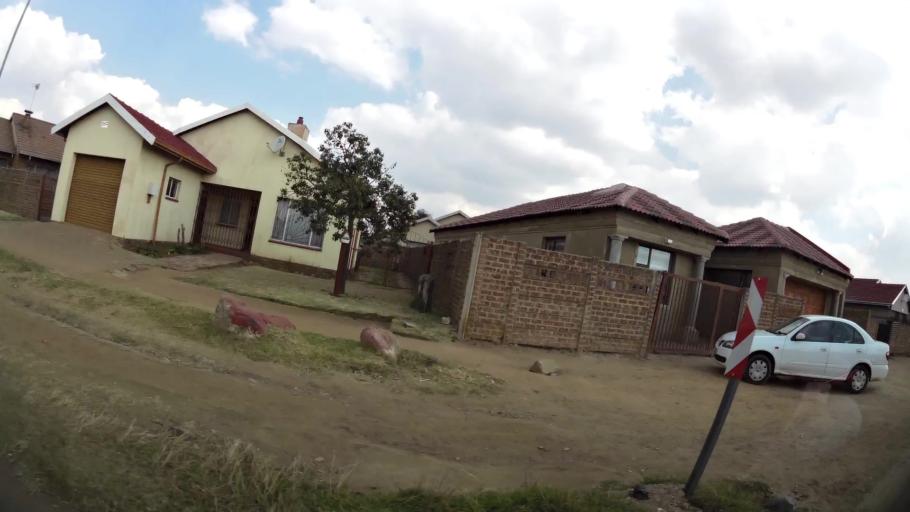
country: ZA
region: Gauteng
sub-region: Ekurhuleni Metropolitan Municipality
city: Brakpan
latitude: -26.1368
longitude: 28.4209
